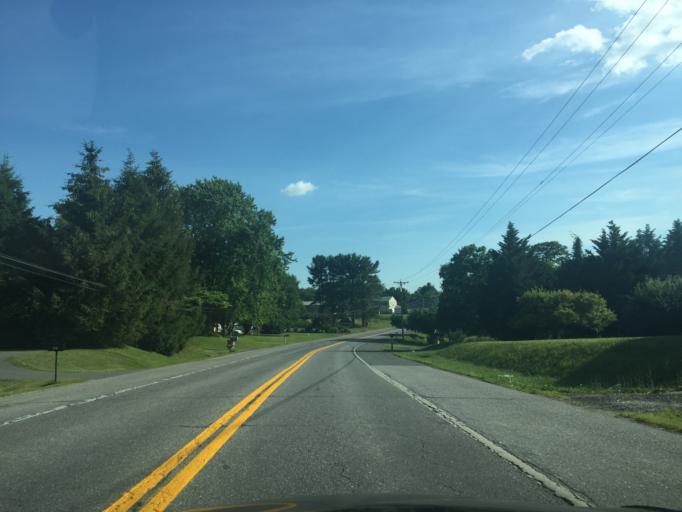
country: US
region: Maryland
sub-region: Harford County
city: Jarrettsville
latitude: 39.6354
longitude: -76.4709
